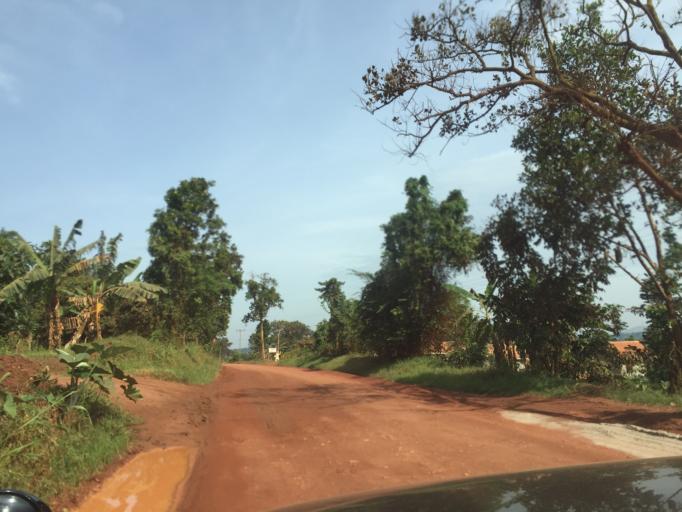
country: UG
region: Central Region
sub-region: Wakiso District
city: Wakiso
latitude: 0.4656
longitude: 32.5411
